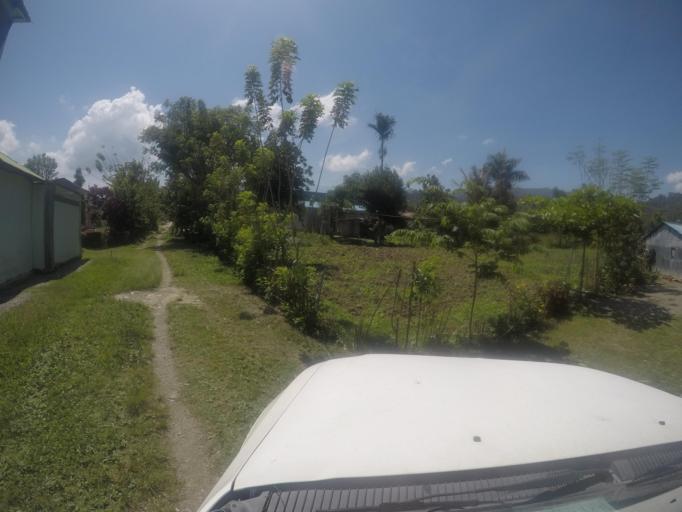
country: TL
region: Ermera
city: Gleno
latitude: -8.7245
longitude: 125.4306
